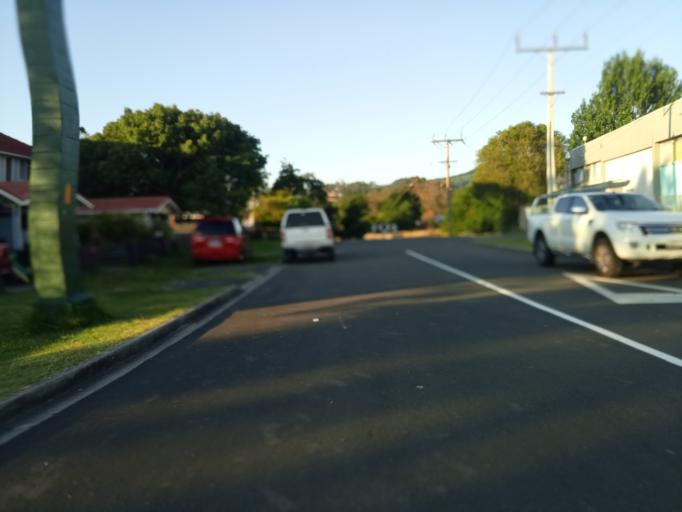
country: NZ
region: Gisborne
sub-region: Gisborne District
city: Gisborne
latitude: -38.6524
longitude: 178.0115
